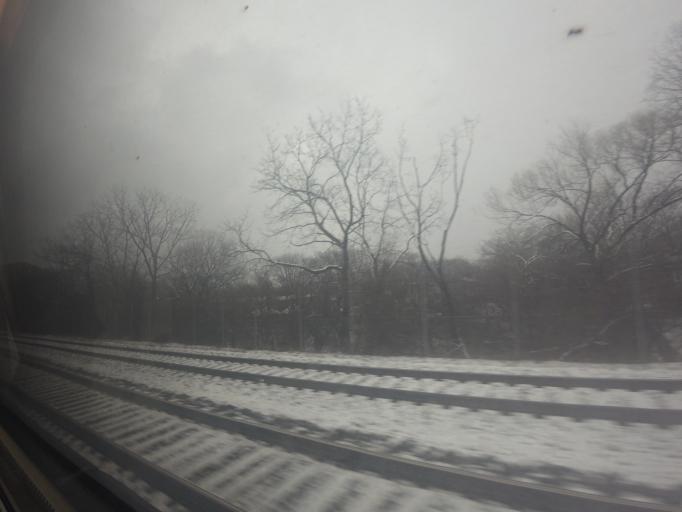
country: CA
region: Ontario
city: Toronto
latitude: 43.6794
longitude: -79.3181
